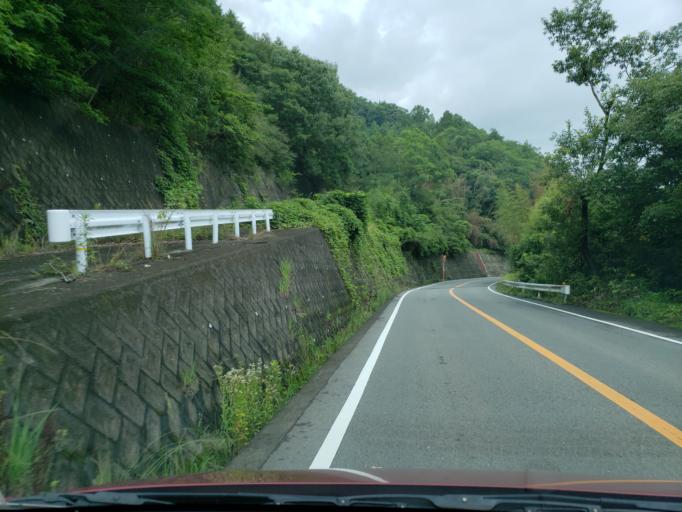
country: JP
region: Tokushima
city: Kamojimacho-jogejima
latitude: 34.1094
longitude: 134.2883
